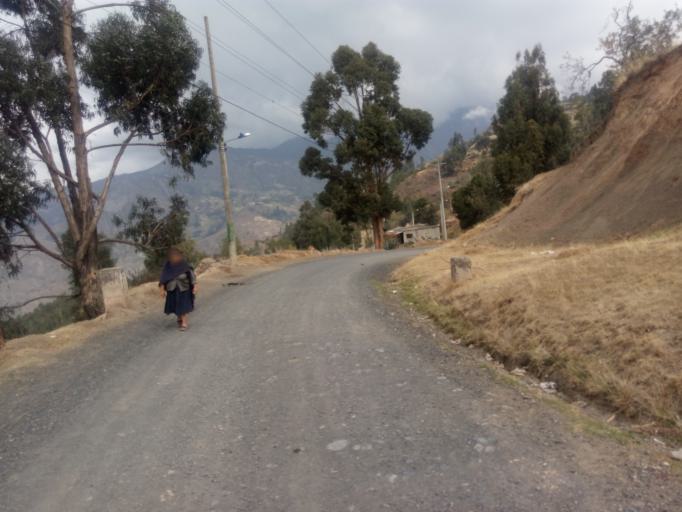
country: CO
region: Boyaca
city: Chita
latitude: 6.1889
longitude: -72.4747
